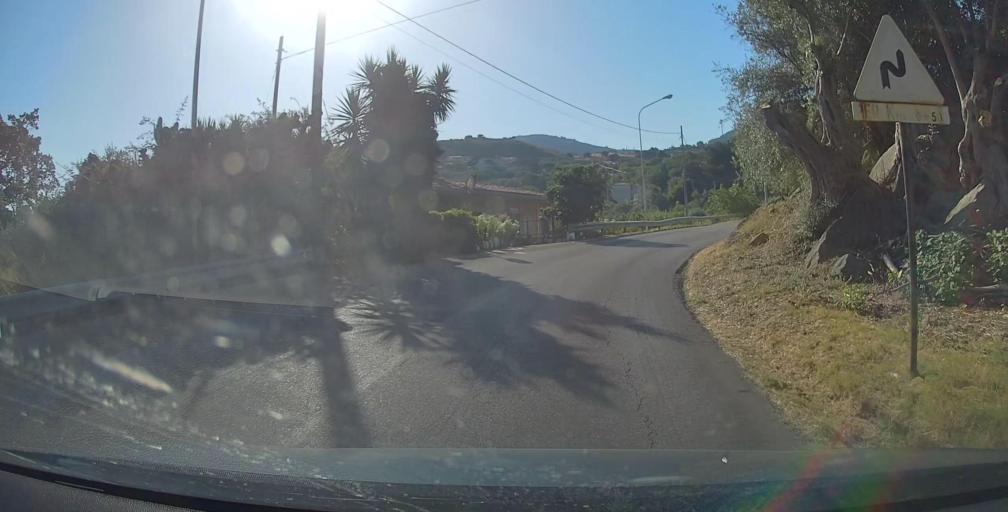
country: IT
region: Sicily
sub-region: Messina
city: Librizzi
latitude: 38.0776
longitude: 14.9757
